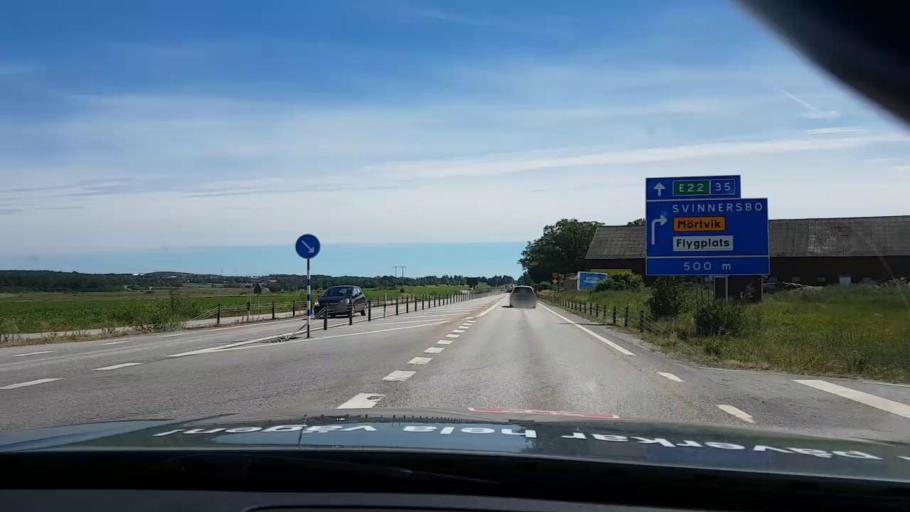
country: SE
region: Kalmar
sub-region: Vasterviks Kommun
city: Vaestervik
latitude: 57.7782
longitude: 16.5386
